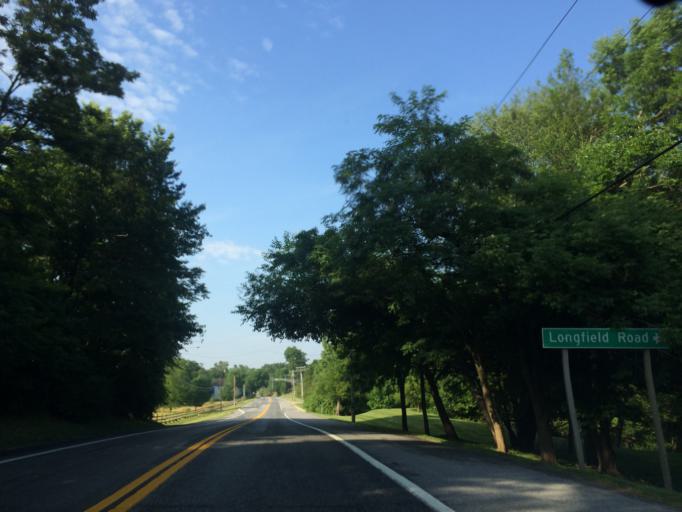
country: US
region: Maryland
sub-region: Carroll County
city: Sykesville
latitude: 39.2873
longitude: -77.0281
